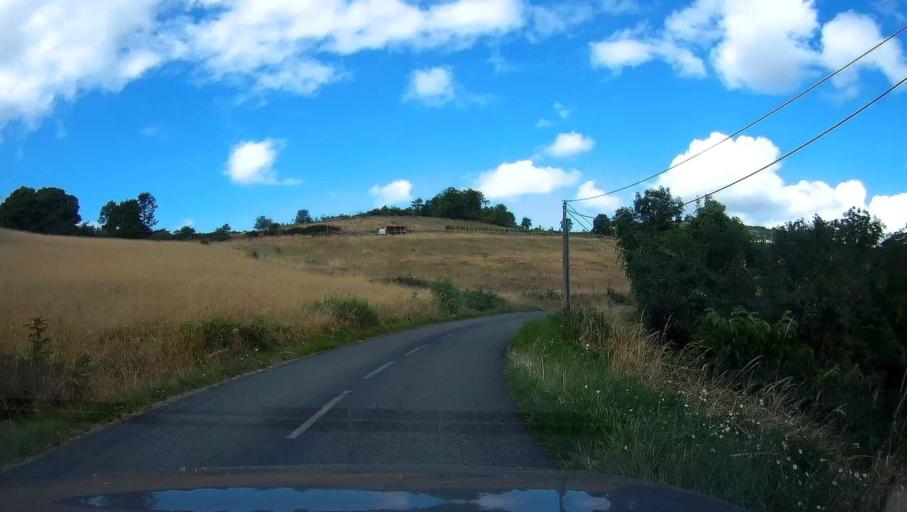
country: FR
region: Rhone-Alpes
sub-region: Departement du Rhone
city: Cogny
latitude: 45.9797
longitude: 4.5926
